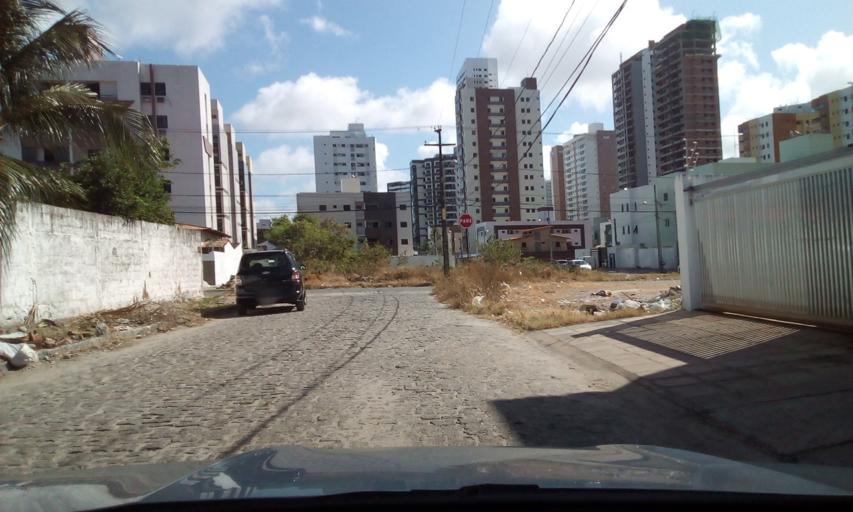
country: BR
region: Paraiba
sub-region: Joao Pessoa
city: Joao Pessoa
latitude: -7.0812
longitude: -34.8366
